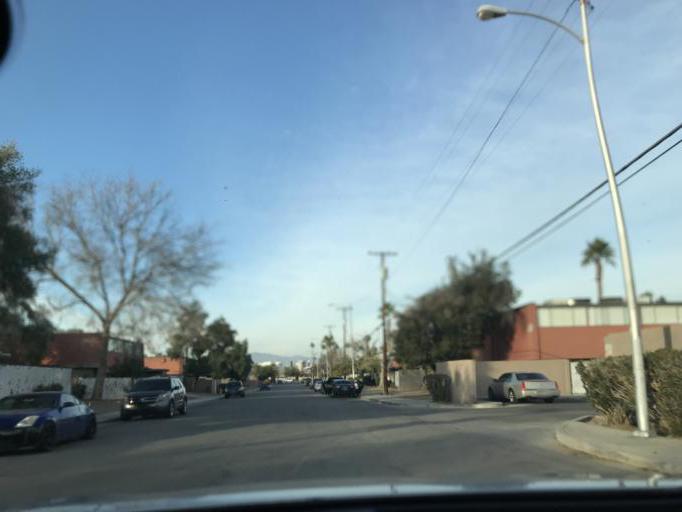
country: US
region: Nevada
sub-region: Clark County
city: Winchester
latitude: 36.1414
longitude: -115.1456
